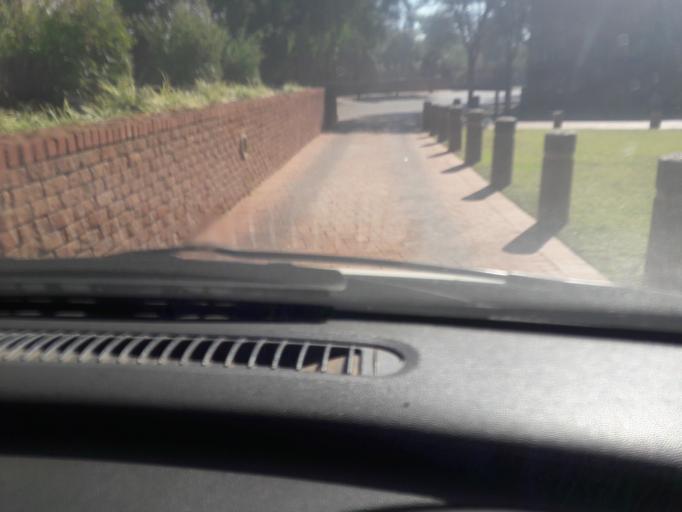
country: ZA
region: Gauteng
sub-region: City of Tshwane Metropolitan Municipality
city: Pretoria
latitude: -25.7664
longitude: 28.2655
